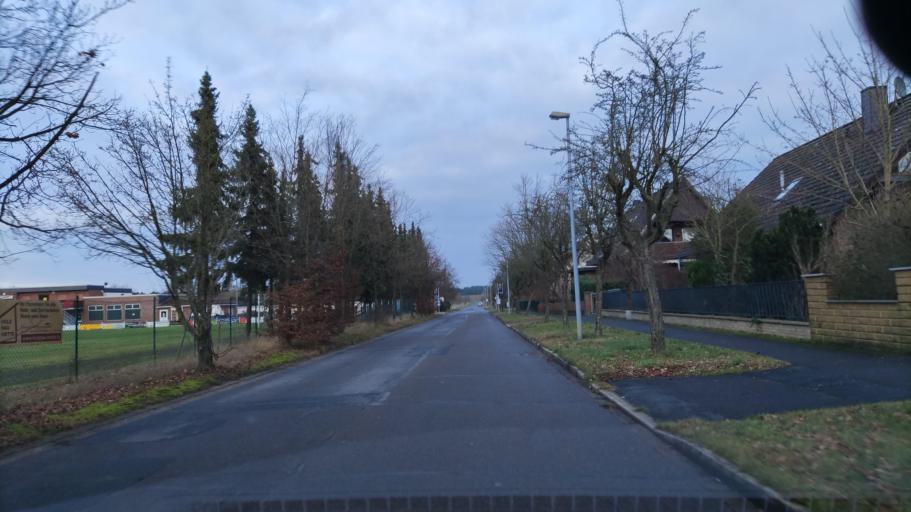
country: DE
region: Lower Saxony
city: Isernhagen Farster Bauerschaft
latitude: 52.5145
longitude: 9.9088
